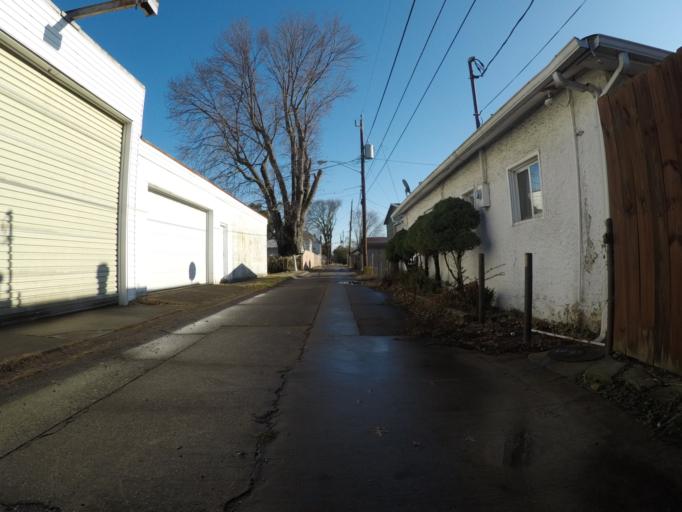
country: US
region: Ohio
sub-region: Lawrence County
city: Burlington
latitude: 38.4094
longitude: -82.4951
